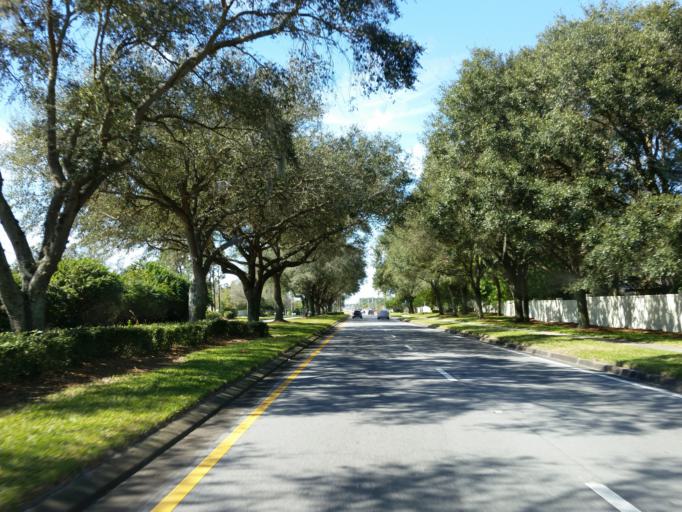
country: US
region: Florida
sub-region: Hillsborough County
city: Balm
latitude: 27.7922
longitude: -82.3251
